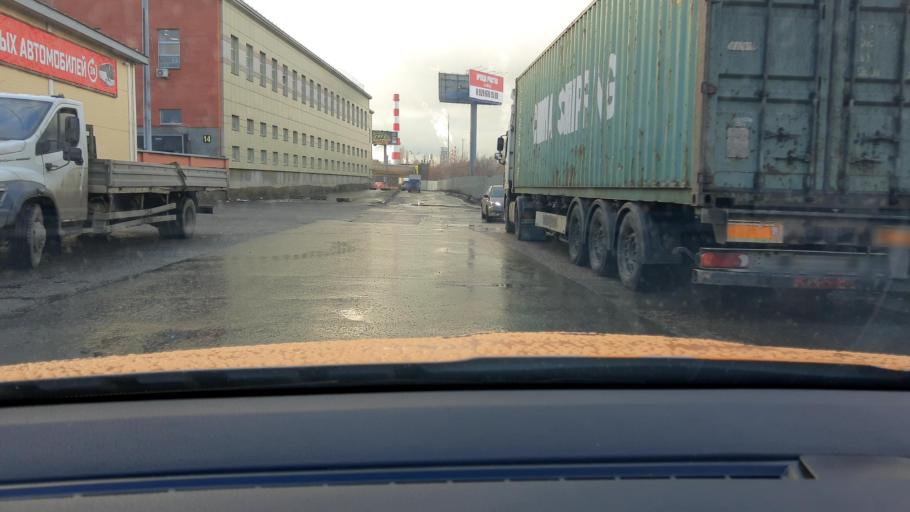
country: RU
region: Moskovskaya
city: Kotel'niki
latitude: 55.6458
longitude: 37.8315
